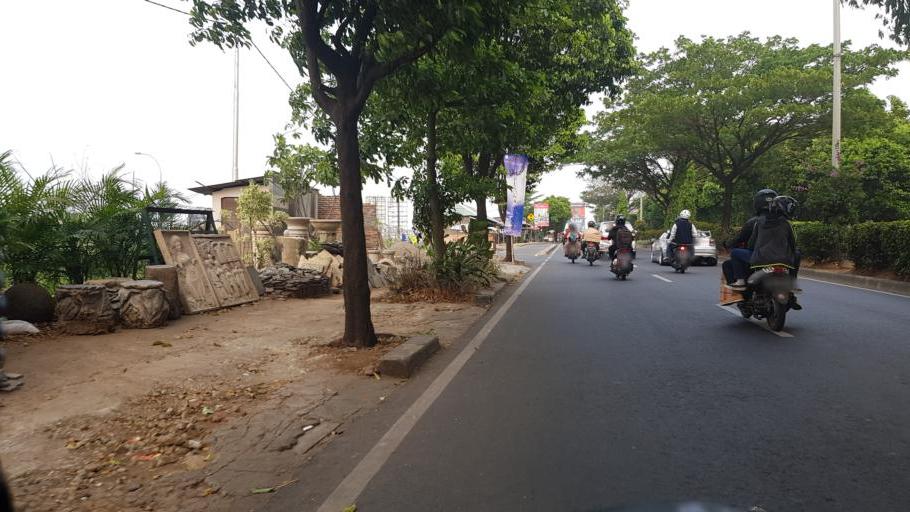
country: ID
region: West Java
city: Depok
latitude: -6.3818
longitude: 106.8646
